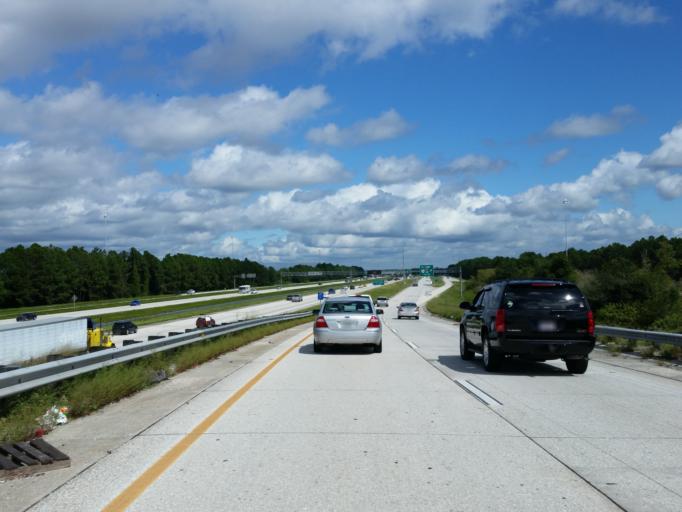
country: US
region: Florida
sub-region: Hillsborough County
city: Progress Village
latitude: 27.9096
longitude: -82.3397
